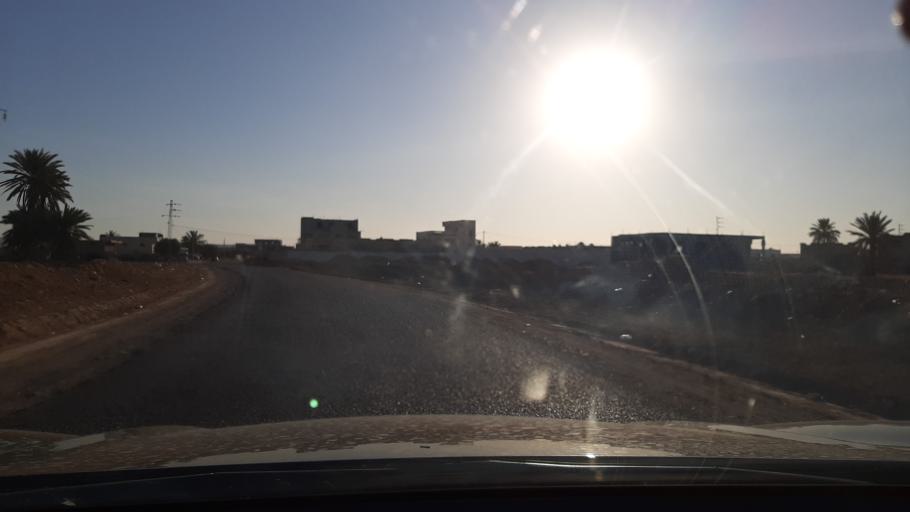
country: TN
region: Qabis
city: Matmata
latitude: 33.6184
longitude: 10.2666
